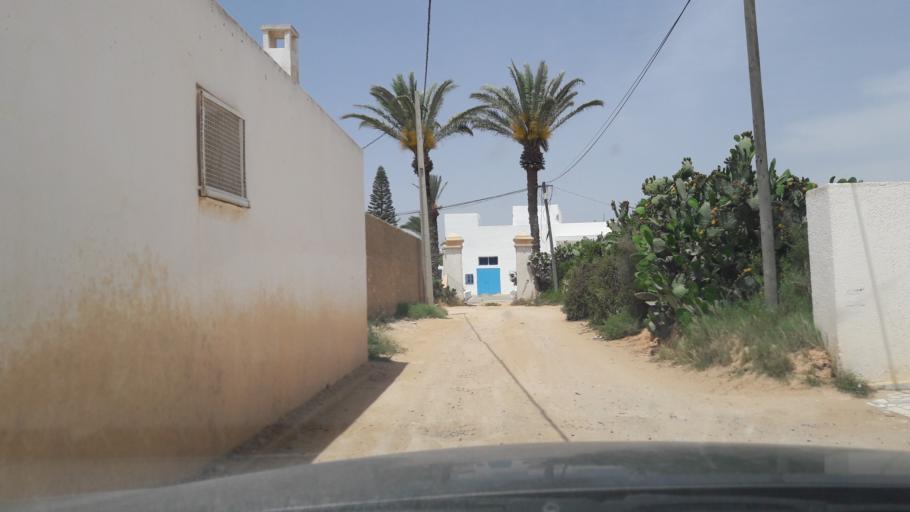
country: TN
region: Safaqis
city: Al Qarmadah
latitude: 34.7836
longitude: 10.7587
